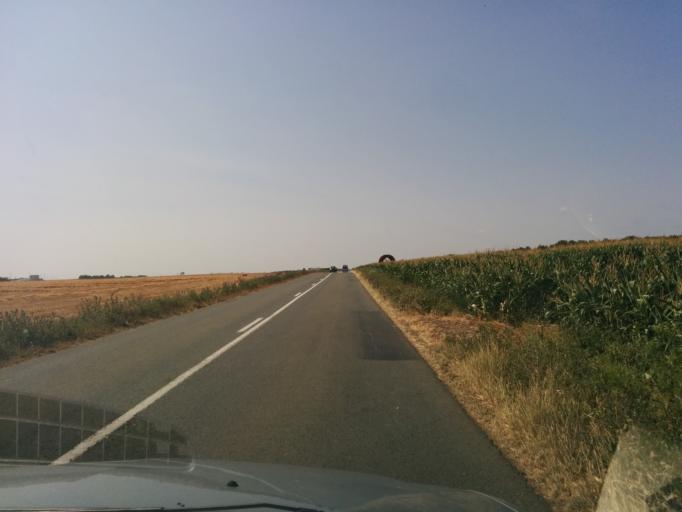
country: FR
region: Poitou-Charentes
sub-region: Departement de la Vienne
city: Mirebeau
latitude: 46.7283
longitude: 0.1976
